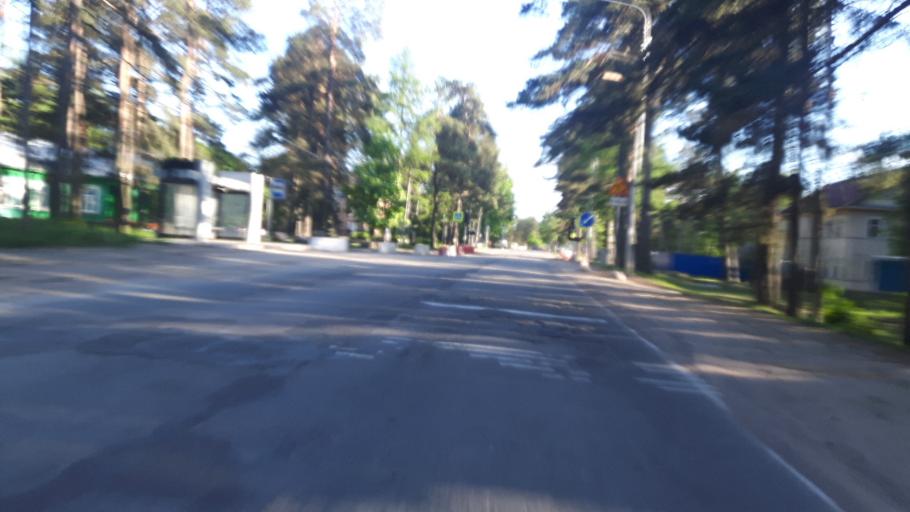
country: RU
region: Leningrad
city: Vistino
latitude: 59.7718
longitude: 28.4748
